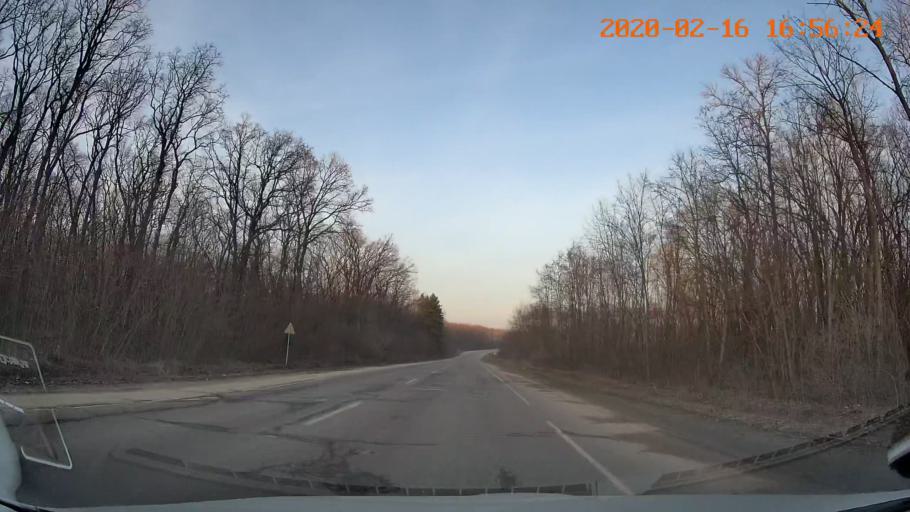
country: MD
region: Briceni
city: Briceni
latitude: 48.3326
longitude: 27.0495
